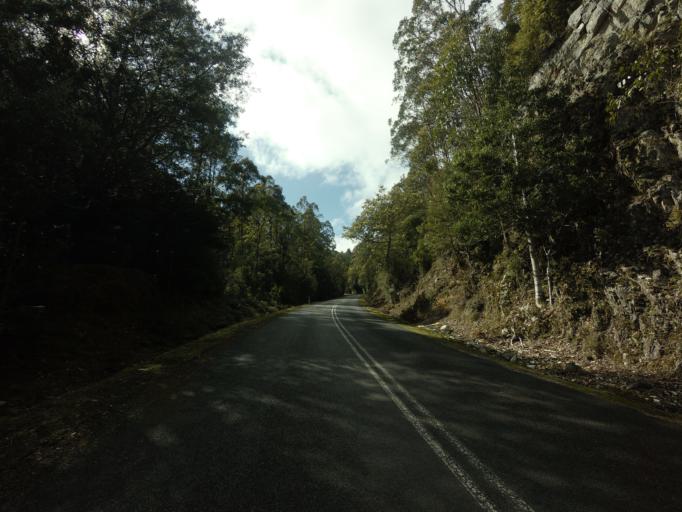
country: AU
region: Tasmania
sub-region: Huon Valley
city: Geeveston
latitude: -42.8175
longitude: 146.3548
